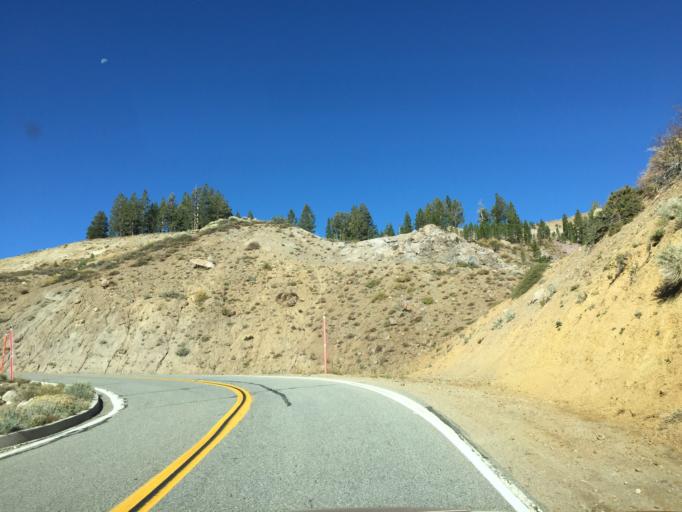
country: US
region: California
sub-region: Mono County
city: Bridgeport
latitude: 38.3289
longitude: -119.6319
